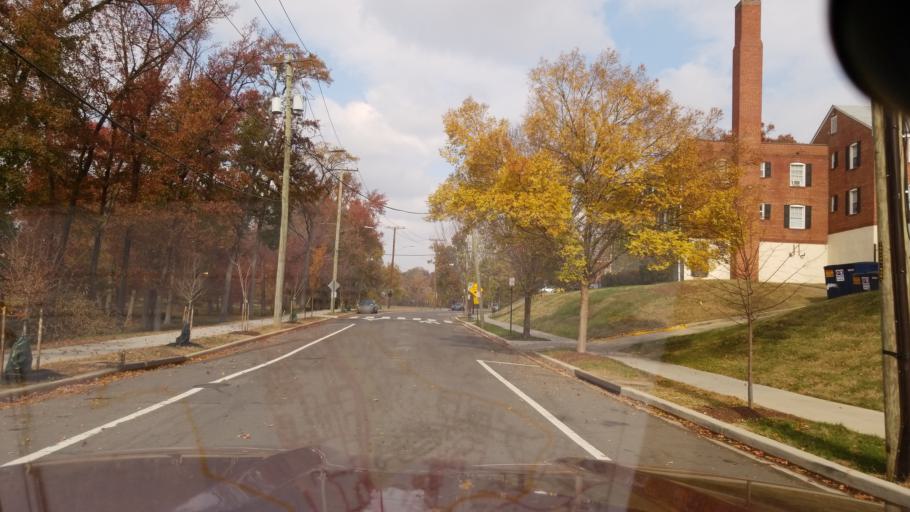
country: US
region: Maryland
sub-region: Prince George's County
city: Glassmanor
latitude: 38.8263
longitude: -77.0036
